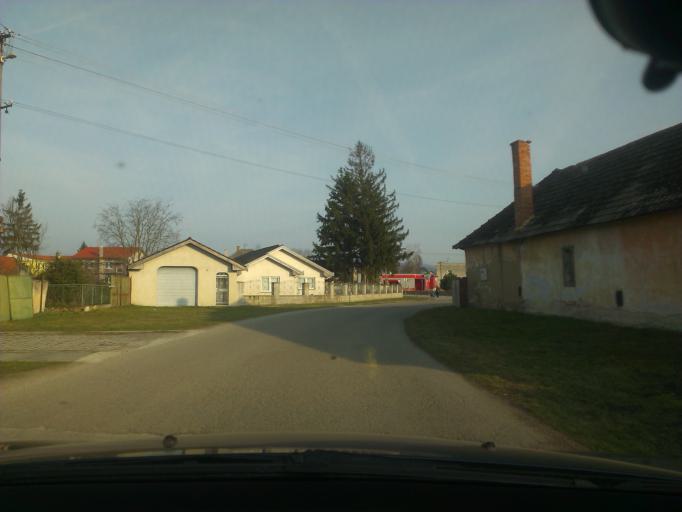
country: SK
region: Trnavsky
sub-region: Okres Trnava
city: Piestany
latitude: 48.6583
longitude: 17.8453
